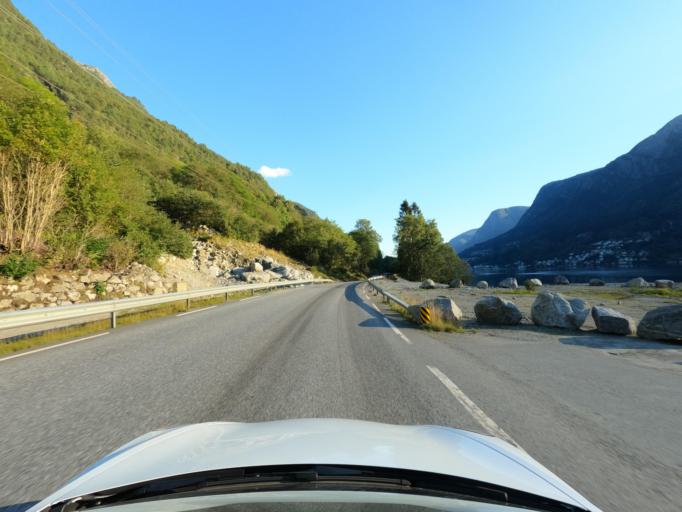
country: NO
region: Hordaland
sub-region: Odda
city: Odda
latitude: 60.0881
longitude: 6.5499
